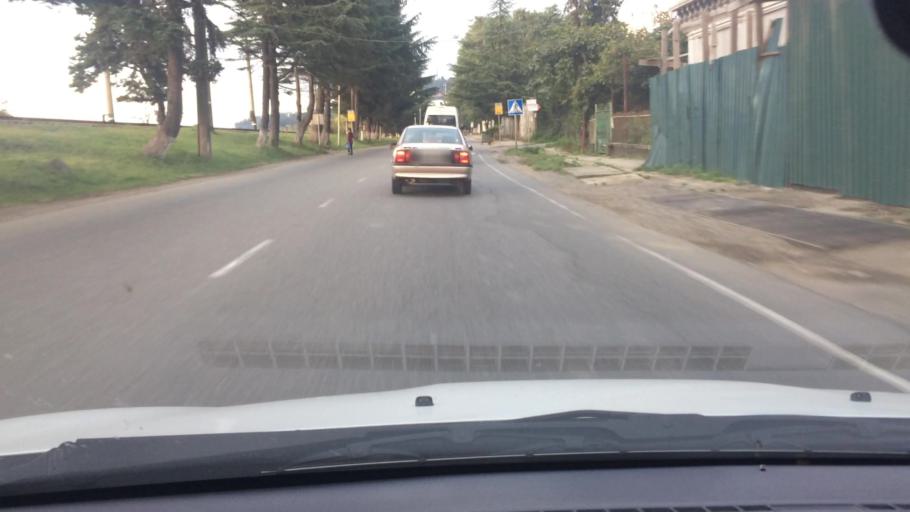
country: GE
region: Ajaria
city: Makhinjauri
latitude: 41.6728
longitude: 41.6919
